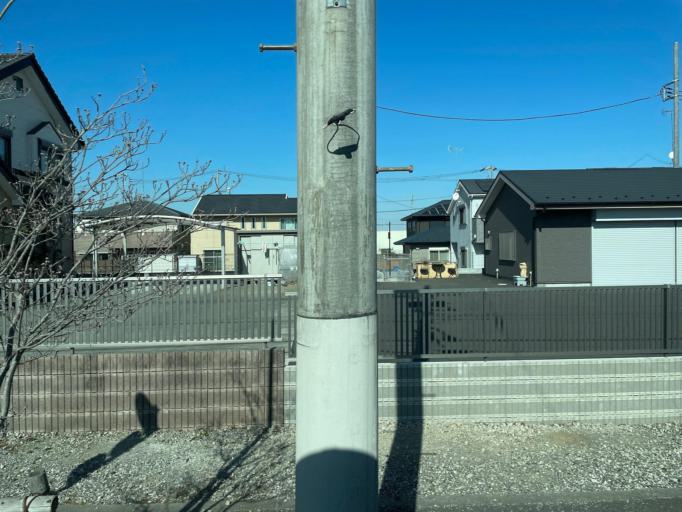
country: JP
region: Tokyo
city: Fussa
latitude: 35.7755
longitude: 139.3436
